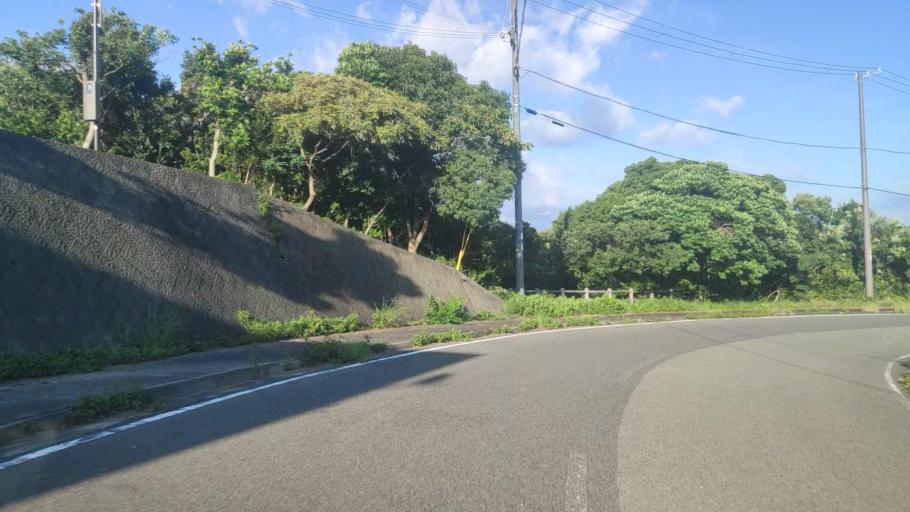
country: JP
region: Wakayama
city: Tanabe
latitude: 33.7752
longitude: 135.3052
